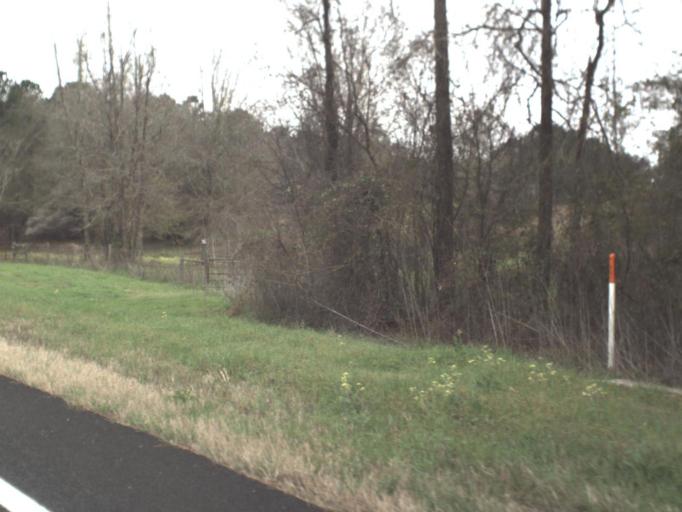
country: US
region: Florida
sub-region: Jefferson County
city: Monticello
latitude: 30.3962
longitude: -83.8741
